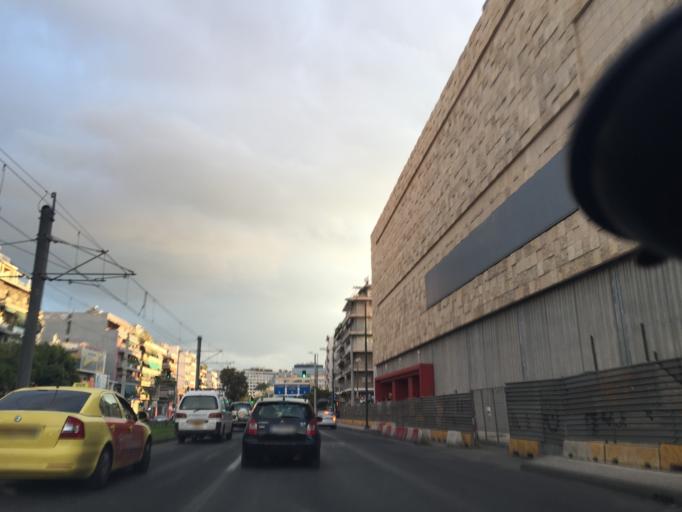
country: GR
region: Attica
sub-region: Nomarchia Athinas
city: Dhafni
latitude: 37.9630
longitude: 23.7257
